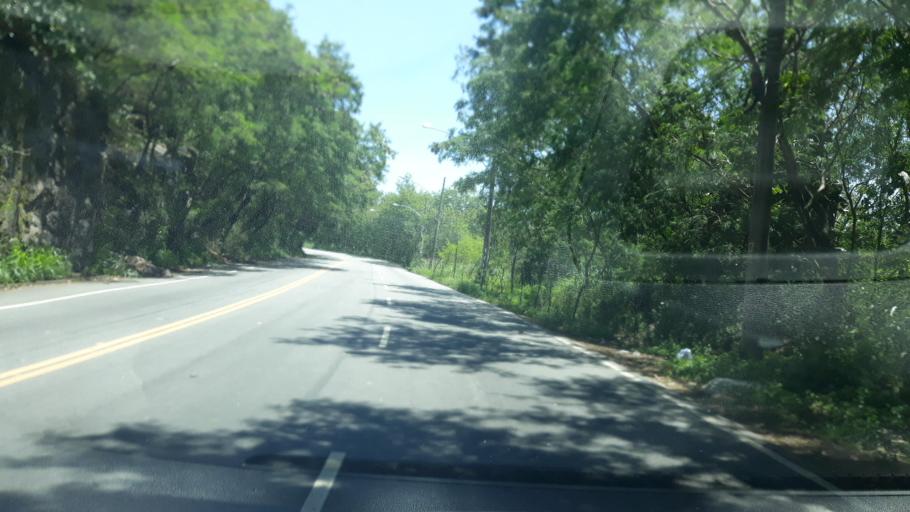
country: BR
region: Rio de Janeiro
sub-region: Nilopolis
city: Nilopolis
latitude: -23.0091
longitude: -43.5132
